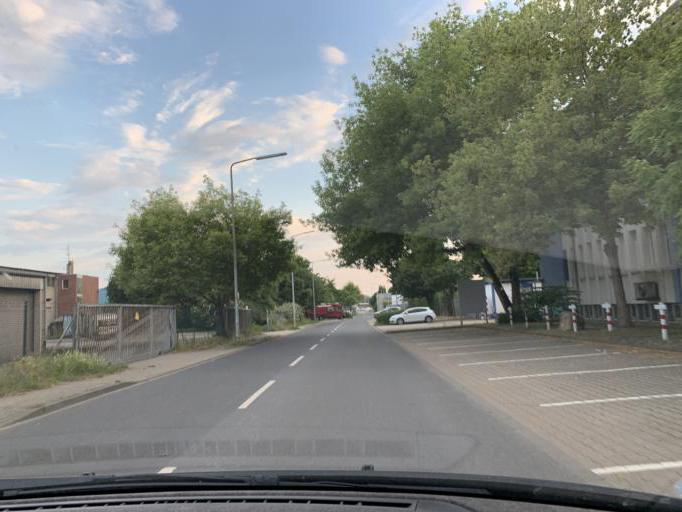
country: DE
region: North Rhine-Westphalia
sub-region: Regierungsbezirk Dusseldorf
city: Dusseldorf
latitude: 51.2146
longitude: 6.7357
